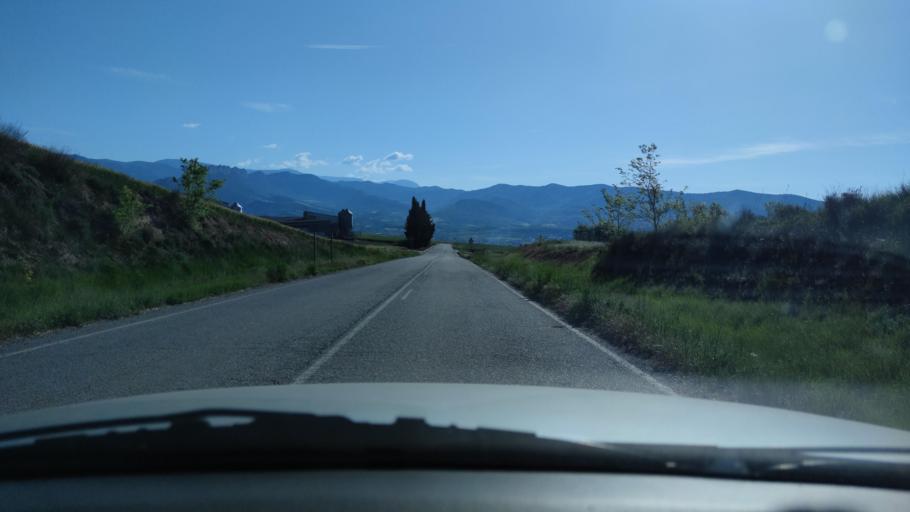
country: ES
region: Catalonia
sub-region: Provincia de Lleida
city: Oliana
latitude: 42.0636
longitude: 1.2790
